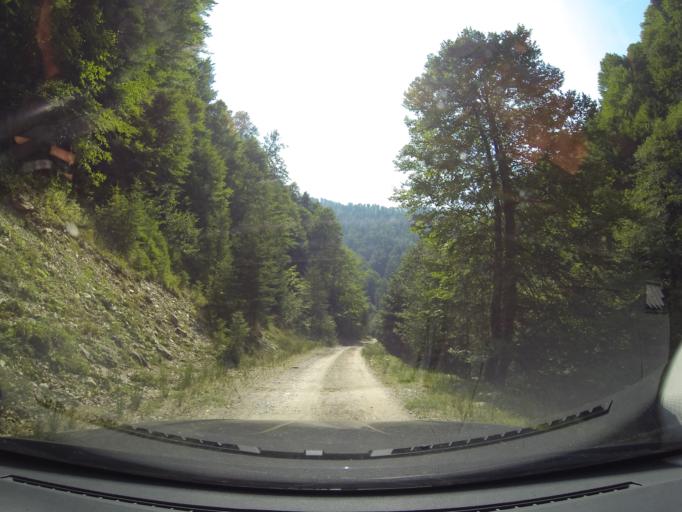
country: RO
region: Arges
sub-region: Comuna Arefu
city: Arefu
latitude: 45.5129
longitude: 24.6687
